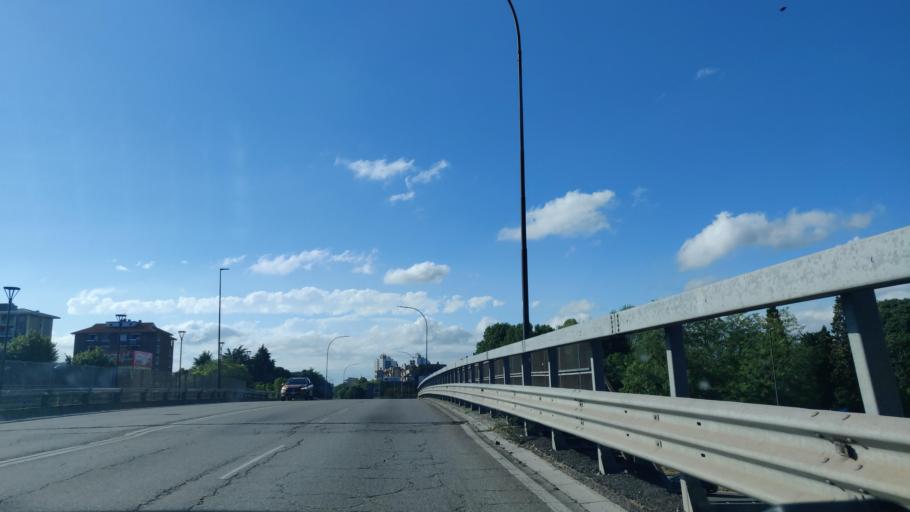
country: IT
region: Lombardy
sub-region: Citta metropolitana di Milano
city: Corsico
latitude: 45.4378
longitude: 9.1055
